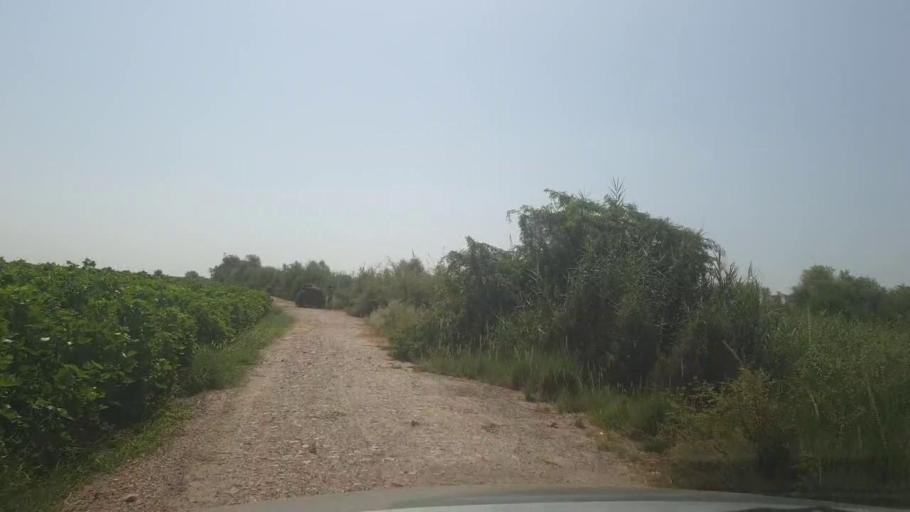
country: PK
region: Sindh
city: Rohri
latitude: 27.4105
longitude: 69.0948
